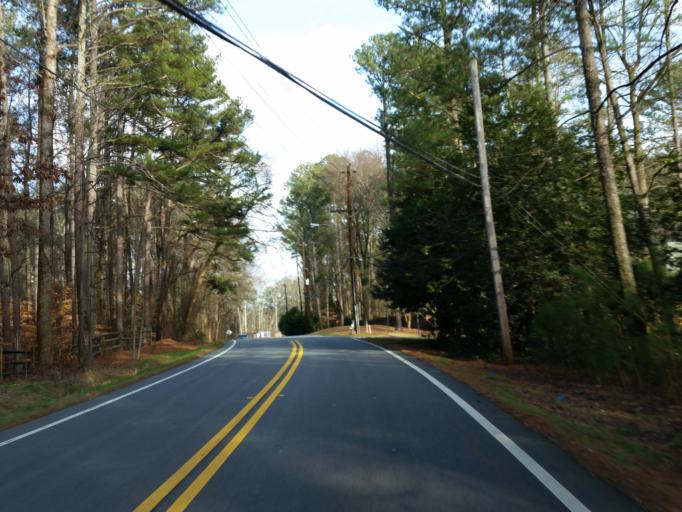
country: US
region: Georgia
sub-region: Fulton County
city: Sandy Springs
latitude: 33.9462
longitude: -84.4312
